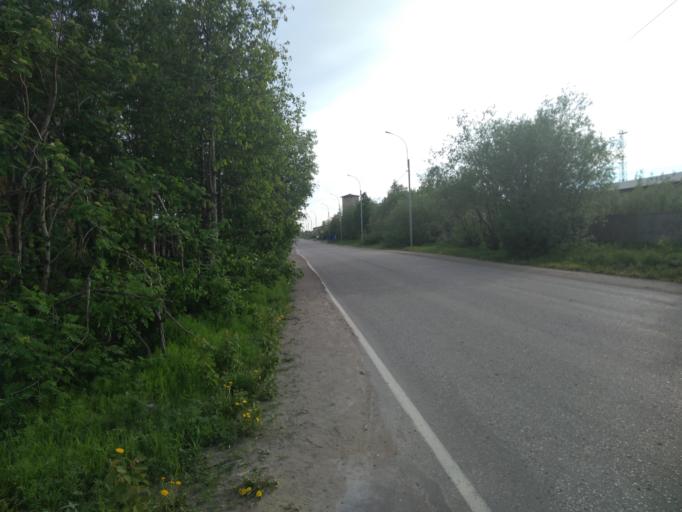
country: RU
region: Komi Republic
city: Pechora
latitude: 65.1495
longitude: 57.2168
